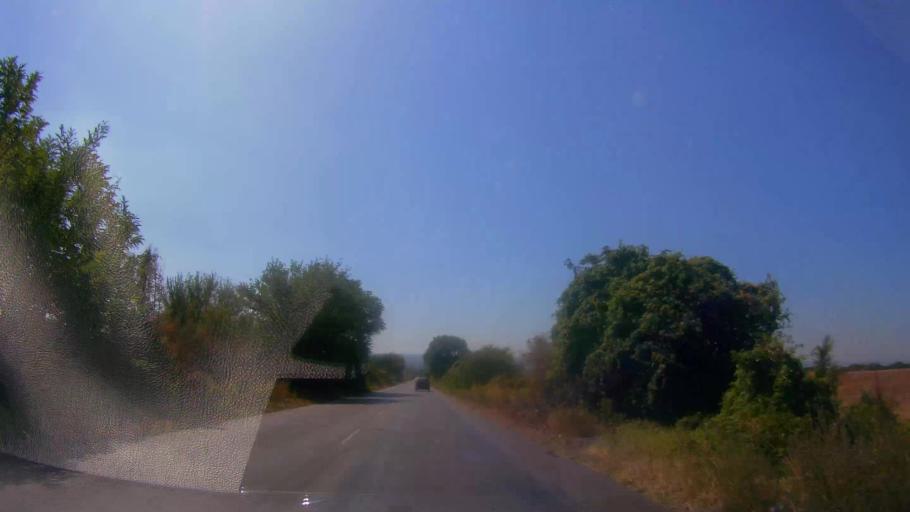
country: BG
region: Veliko Turnovo
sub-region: Obshtina Gorna Oryakhovitsa
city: Purvomaytsi
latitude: 43.2279
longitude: 25.6391
